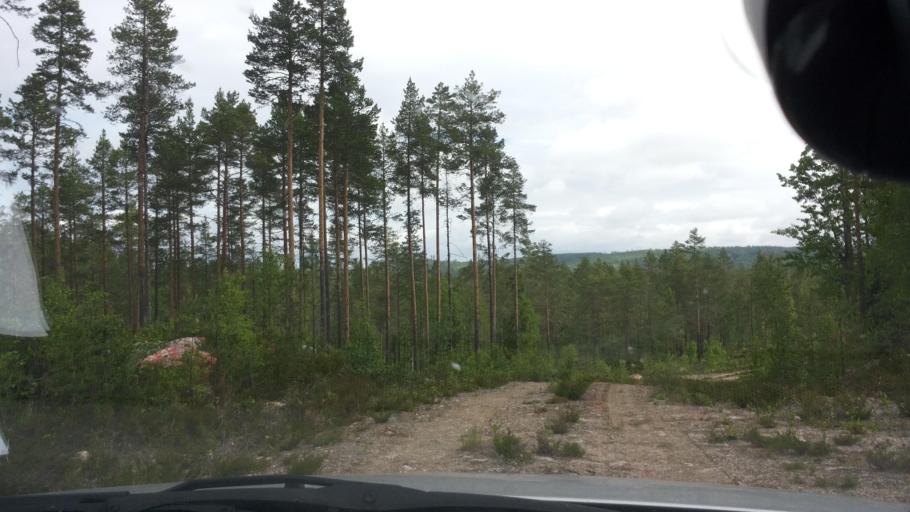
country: SE
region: Gaevleborg
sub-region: Ovanakers Kommun
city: Edsbyn
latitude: 61.4530
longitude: 15.3195
